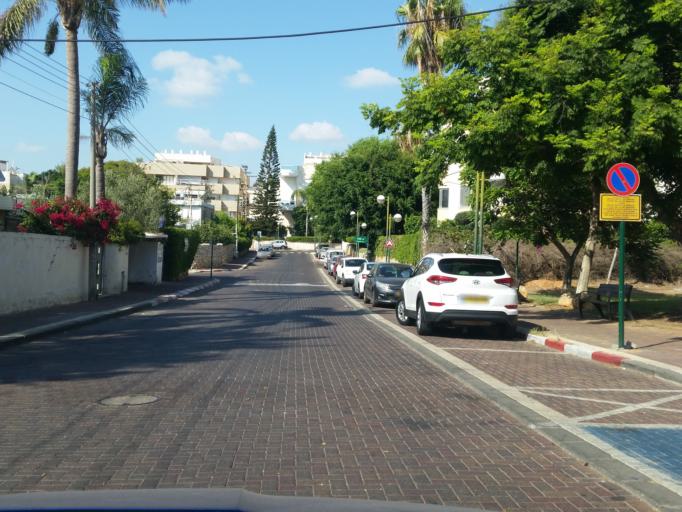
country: IL
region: Tel Aviv
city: Ramat HaSharon
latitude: 32.1394
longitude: 34.8391
